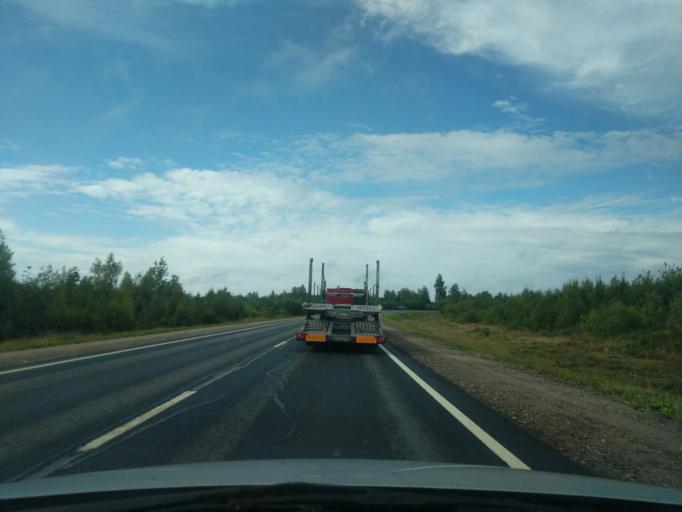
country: RU
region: Kostroma
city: Sudislavl'
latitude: 57.8220
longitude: 41.9037
